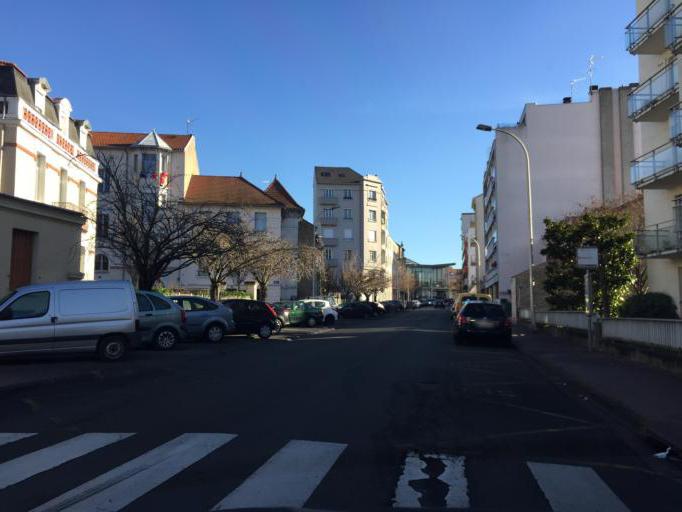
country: FR
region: Auvergne
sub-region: Departement de l'Allier
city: Vichy
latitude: 46.1306
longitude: 3.4213
